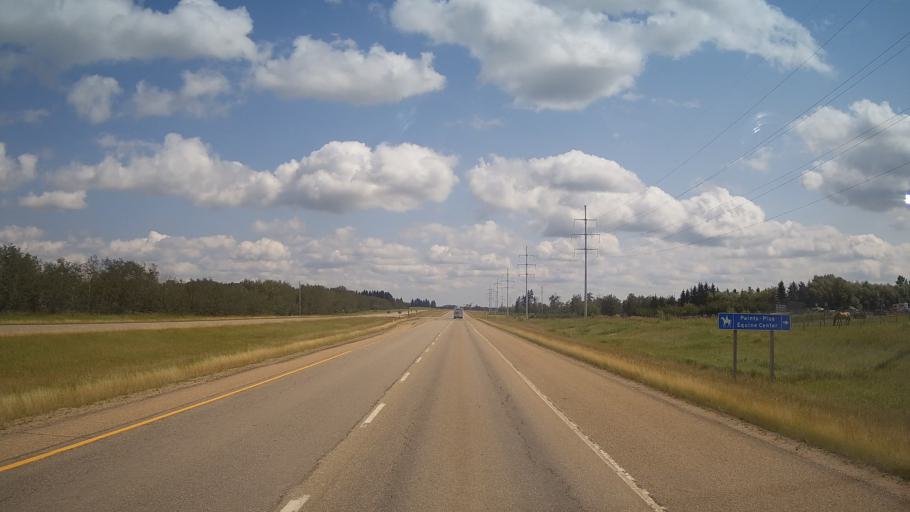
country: CA
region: Alberta
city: Sherwood Park
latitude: 53.4398
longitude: -113.2131
